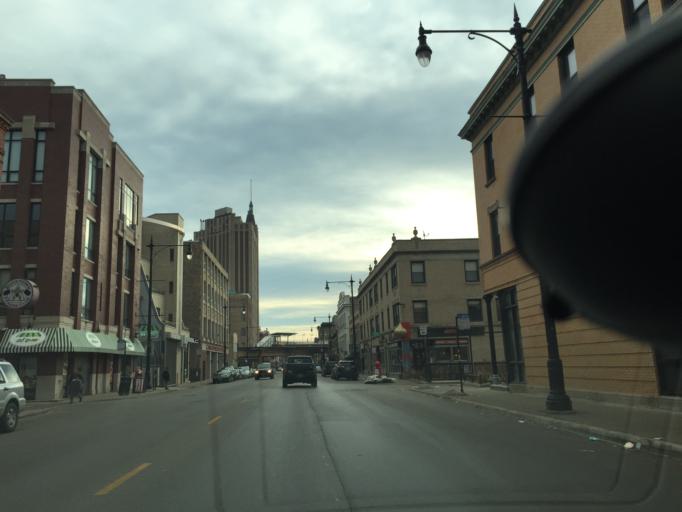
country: US
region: Illinois
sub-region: Cook County
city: Chicago
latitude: 41.9105
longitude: -87.6804
